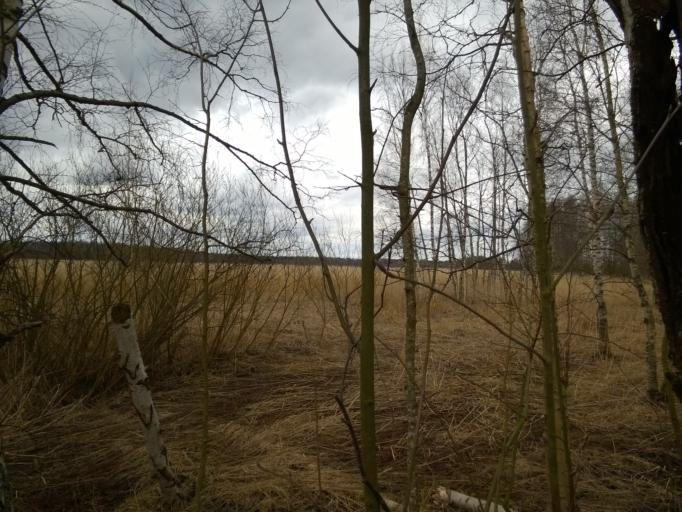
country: FI
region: Uusimaa
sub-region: Helsinki
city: Helsinki
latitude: 60.2178
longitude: 24.9905
